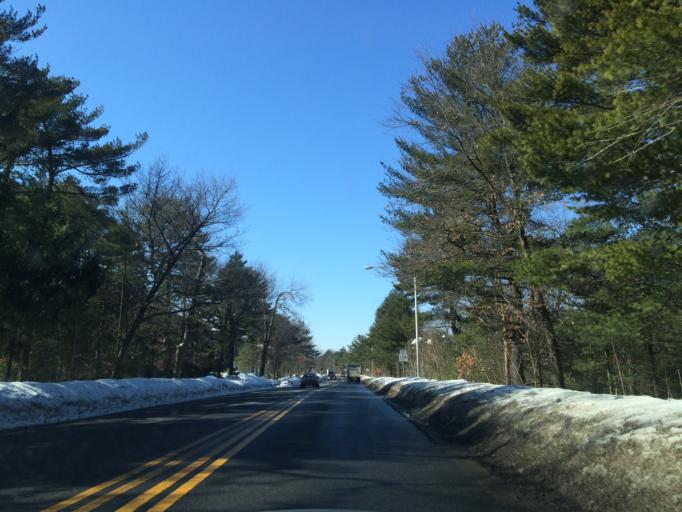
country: US
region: Massachusetts
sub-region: Norfolk County
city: Wellesley
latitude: 42.2962
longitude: -71.3096
